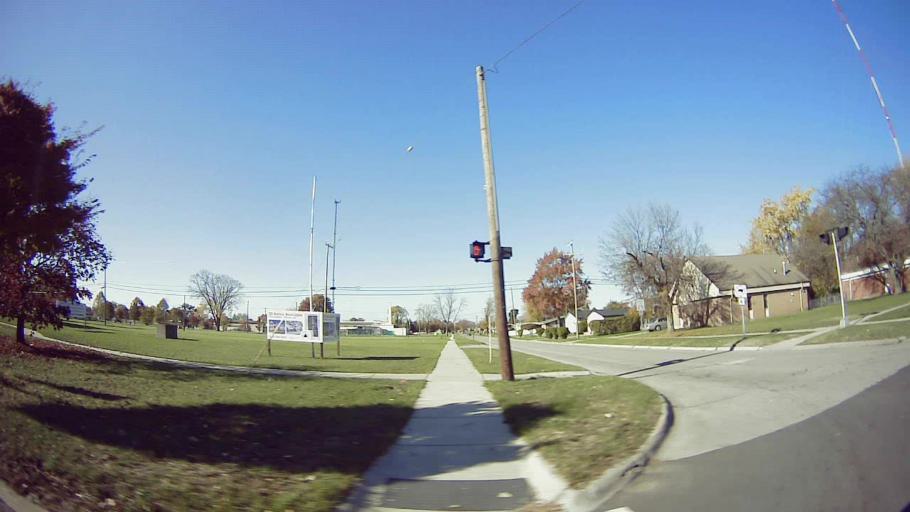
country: US
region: Michigan
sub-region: Oakland County
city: Oak Park
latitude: 42.4506
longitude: -83.1617
